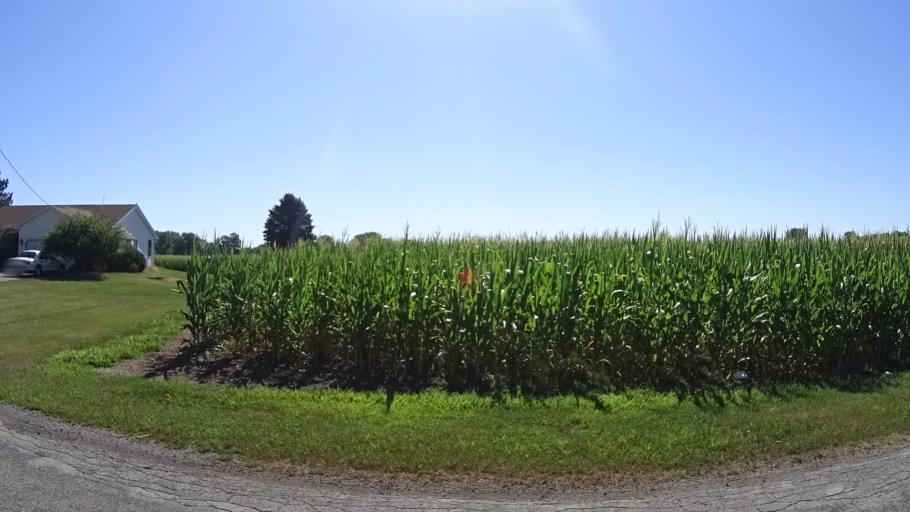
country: US
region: Ohio
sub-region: Erie County
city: Sandusky
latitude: 41.3812
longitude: -82.7057
